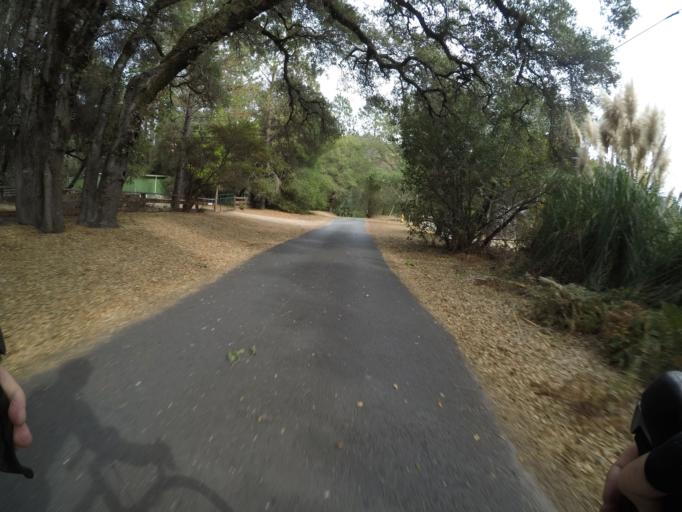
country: US
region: California
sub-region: Santa Cruz County
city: Mount Hermon
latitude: 37.0718
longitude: -122.0593
